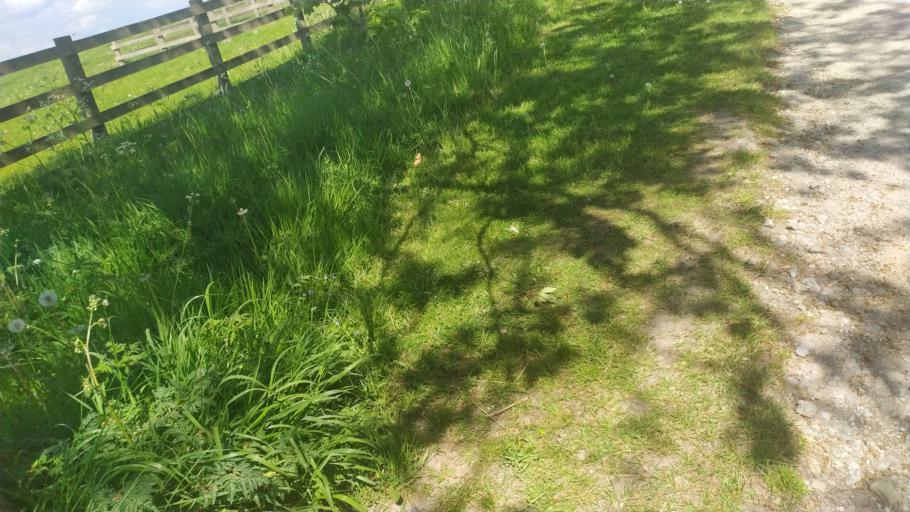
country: GB
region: England
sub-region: City and Borough of Leeds
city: Chapel Allerton
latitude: 53.8940
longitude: -1.5351
